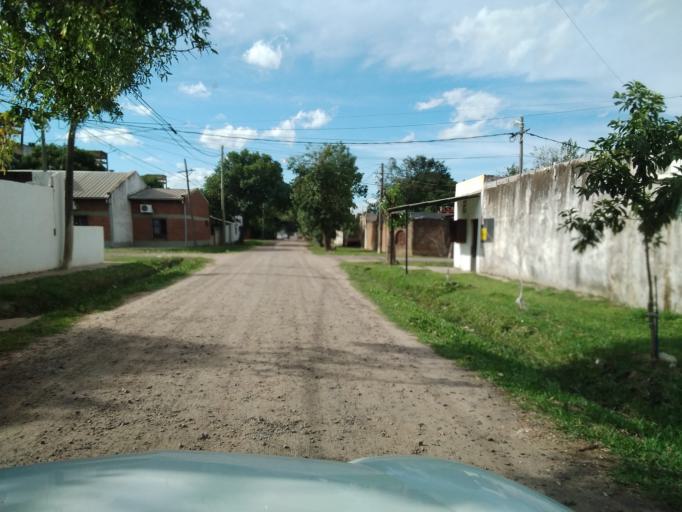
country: AR
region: Corrientes
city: Corrientes
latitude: -27.4865
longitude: -58.8432
